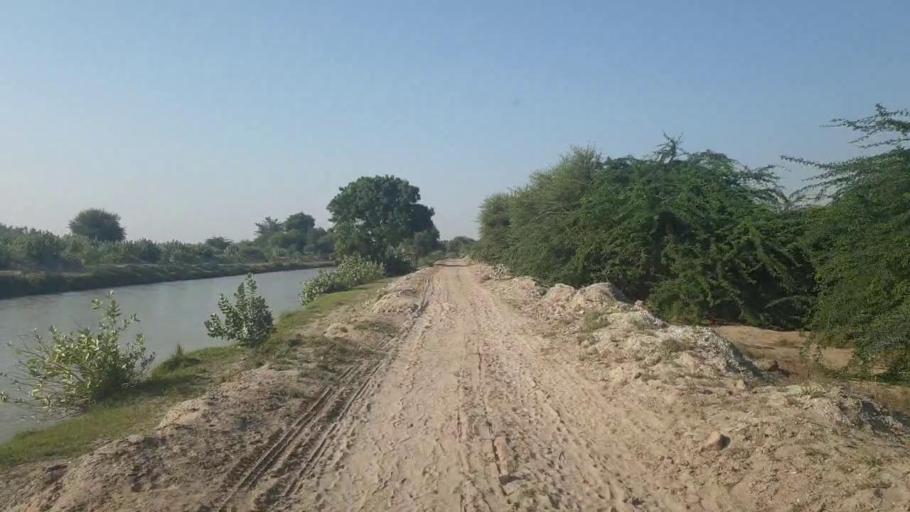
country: PK
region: Sindh
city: Tando Bago
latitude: 24.7201
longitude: 68.9172
